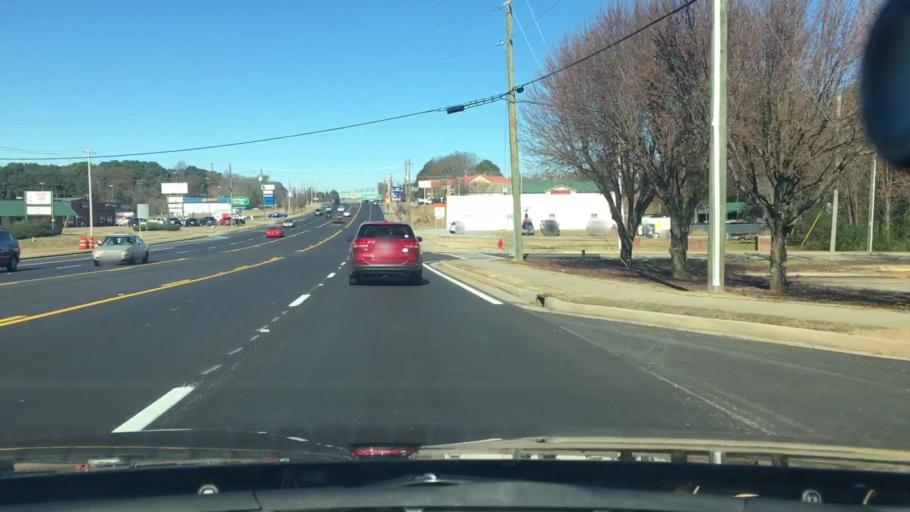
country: US
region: Georgia
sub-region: Spalding County
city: Experiment
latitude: 33.2569
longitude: -84.2882
